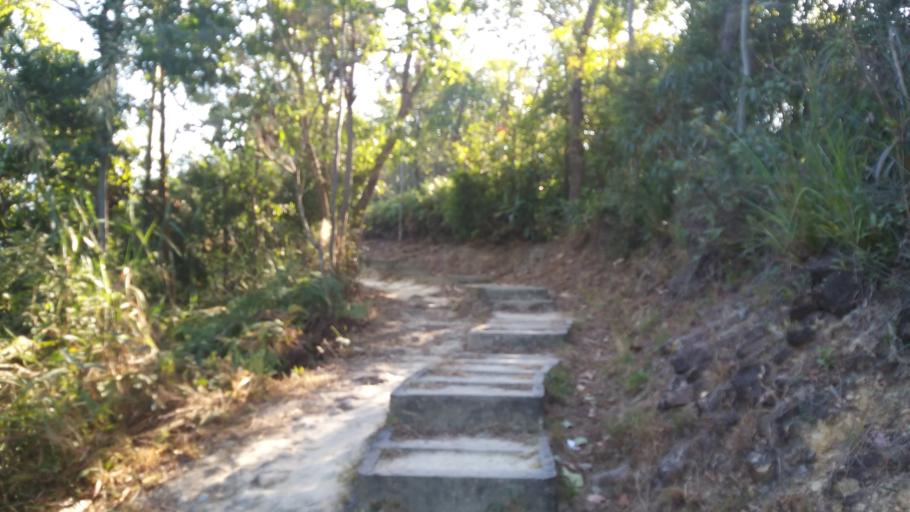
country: HK
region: Tuen Mun
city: Tuen Mun
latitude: 22.4063
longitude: 113.9887
